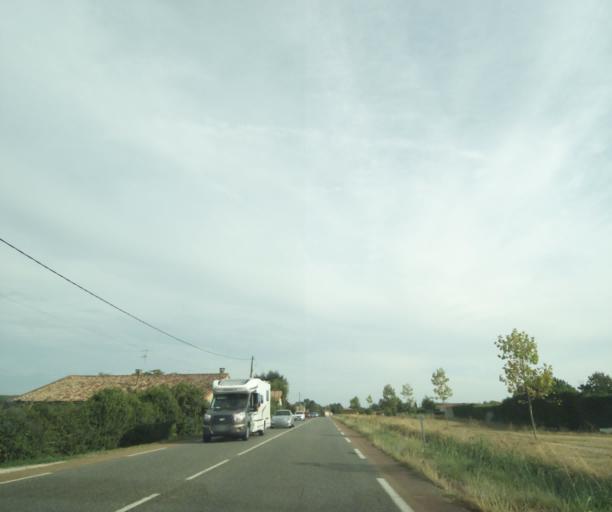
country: FR
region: Midi-Pyrenees
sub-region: Departement du Tarn-et-Garonne
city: Verdun-sur-Garonne
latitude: 43.8679
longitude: 1.2659
